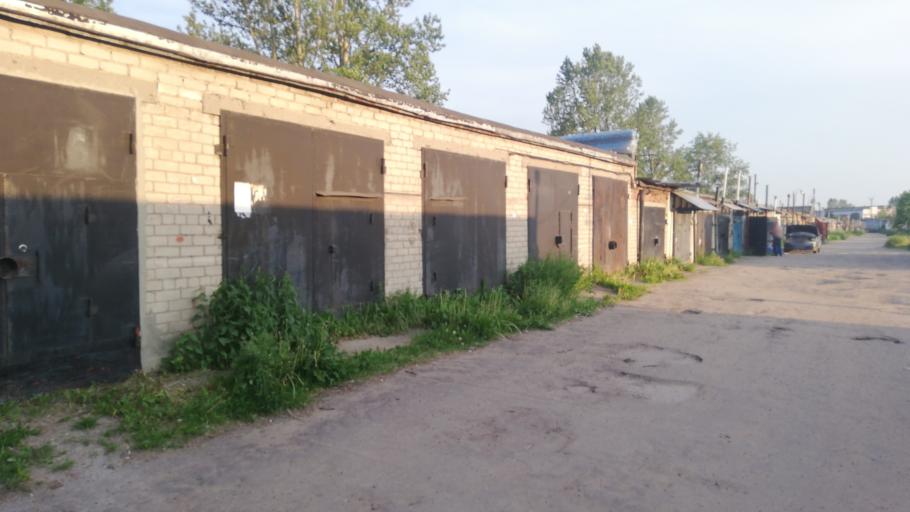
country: RU
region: Jaroslavl
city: Yaroslavl
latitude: 57.5775
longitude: 39.8371
